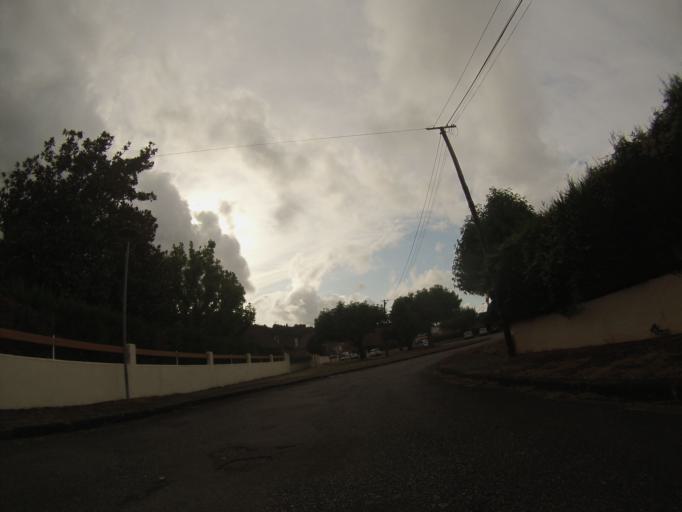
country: FR
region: Aquitaine
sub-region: Departement des Pyrenees-Atlantiques
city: Gelos
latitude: 43.2797
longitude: -0.3724
